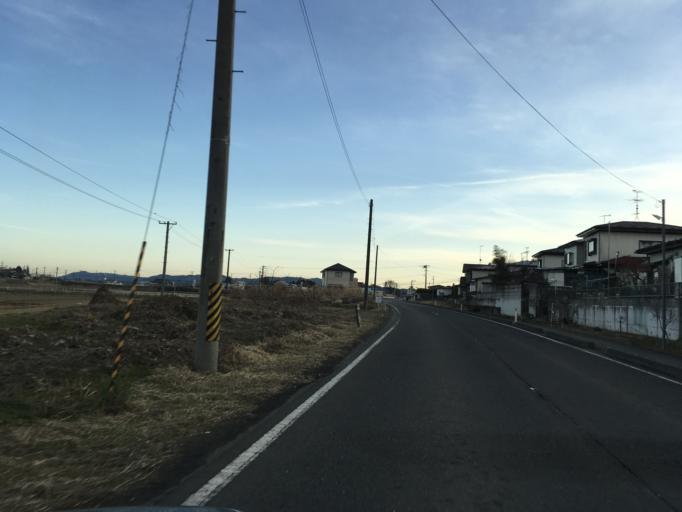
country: JP
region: Miyagi
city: Kogota
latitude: 38.6537
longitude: 141.0749
